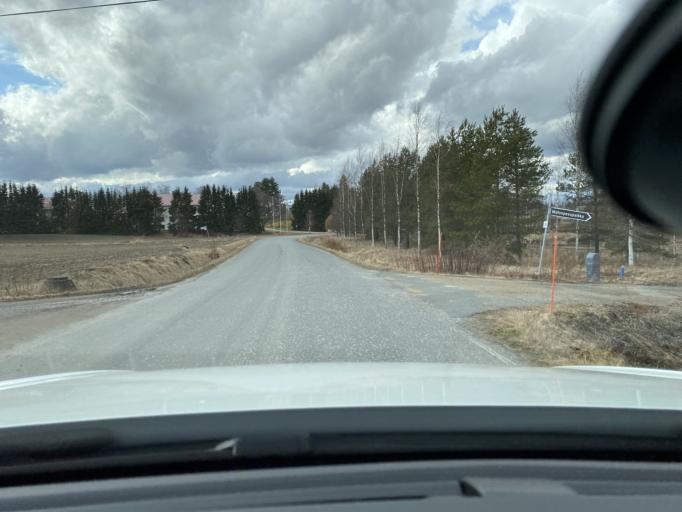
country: FI
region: Pirkanmaa
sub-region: Lounais-Pirkanmaa
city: Punkalaidun
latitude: 61.1191
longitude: 23.0540
